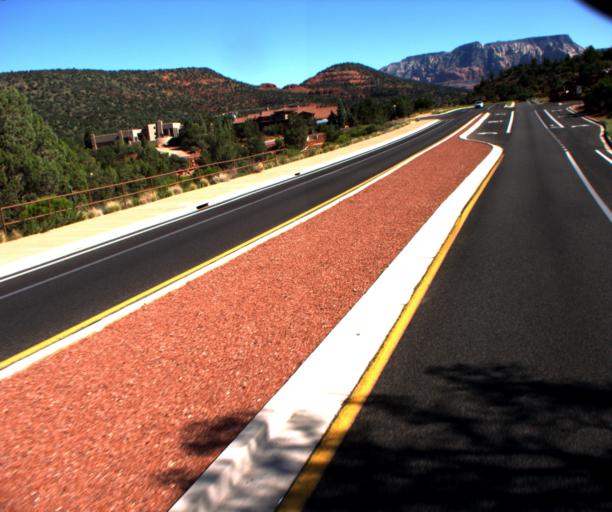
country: US
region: Arizona
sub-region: Coconino County
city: Sedona
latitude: 34.8385
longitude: -111.7767
